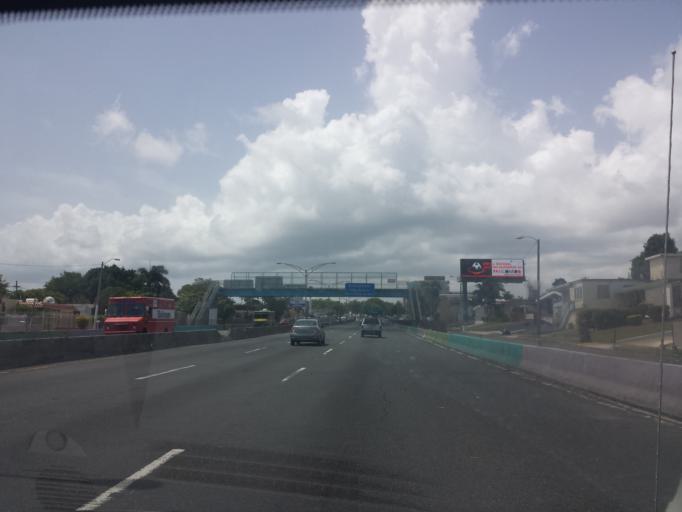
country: PR
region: Guaynabo
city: Guaynabo
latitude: 18.3999
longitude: -66.1051
